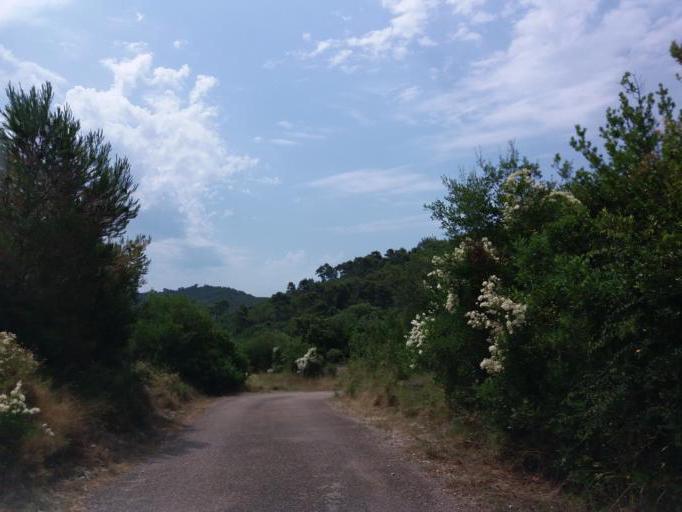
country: HR
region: Zadarska
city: Sali
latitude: 43.9181
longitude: 15.1256
